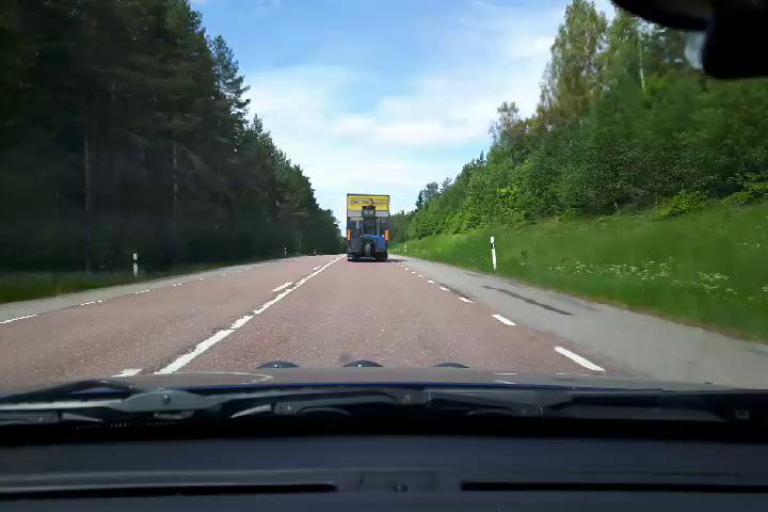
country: SE
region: Uppsala
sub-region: Osthammars Kommun
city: Bjorklinge
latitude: 60.1373
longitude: 17.5063
